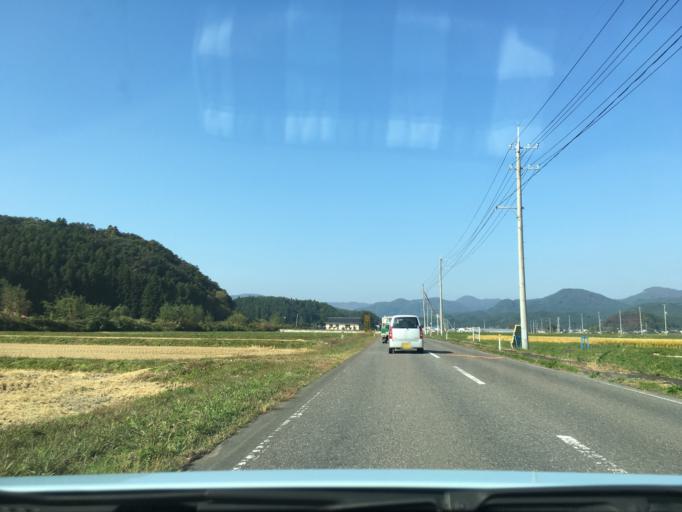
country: JP
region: Fukushima
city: Sukagawa
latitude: 37.2876
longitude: 140.2306
